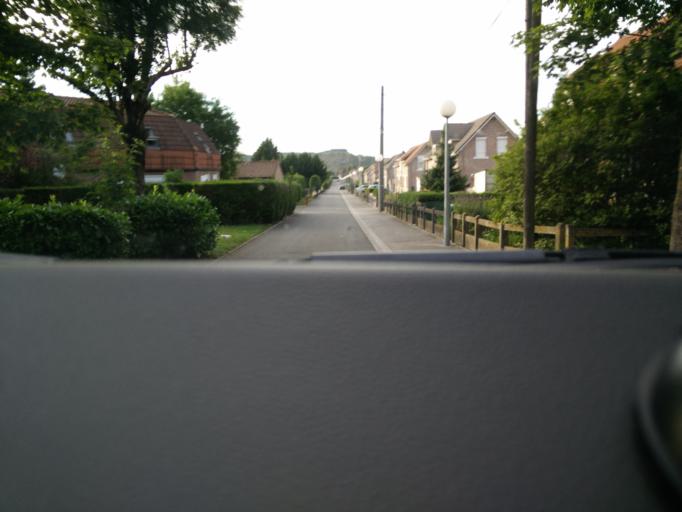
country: FR
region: Nord-Pas-de-Calais
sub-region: Departement du Pas-de-Calais
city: Grenay
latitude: 50.4493
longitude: 2.7487
